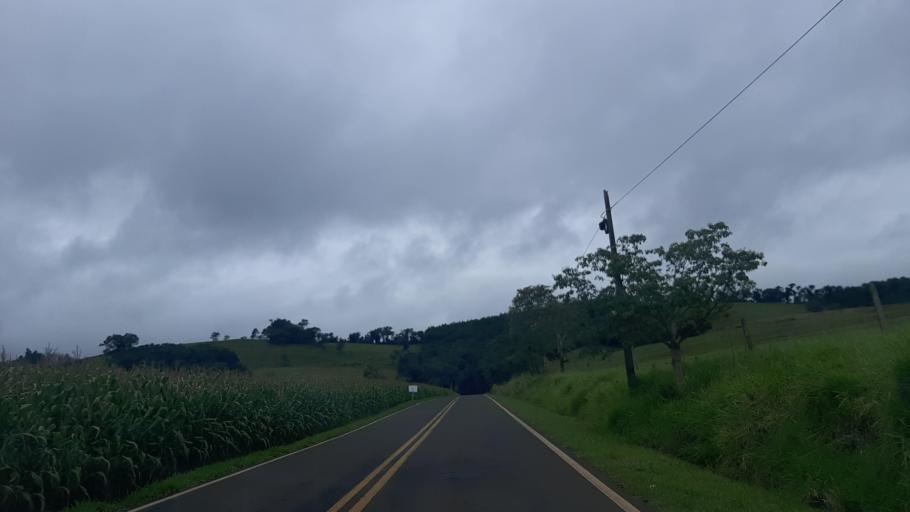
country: BR
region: Parana
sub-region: Ampere
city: Ampere
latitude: -25.9813
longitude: -53.4438
